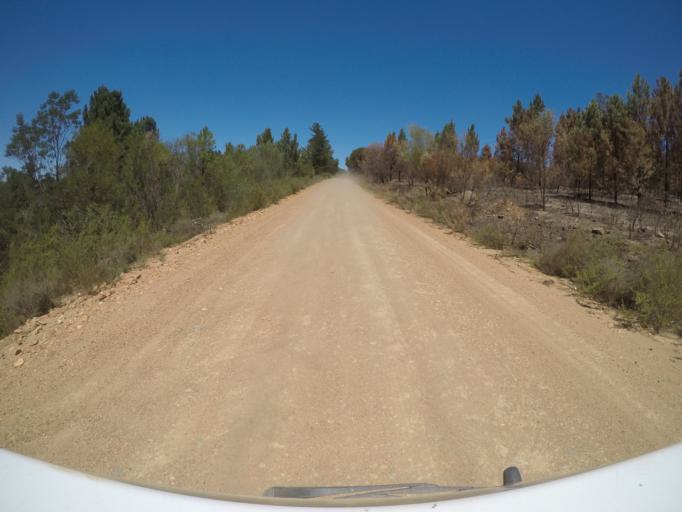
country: ZA
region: Western Cape
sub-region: Overberg District Municipality
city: Grabouw
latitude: -34.1610
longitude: 19.2254
